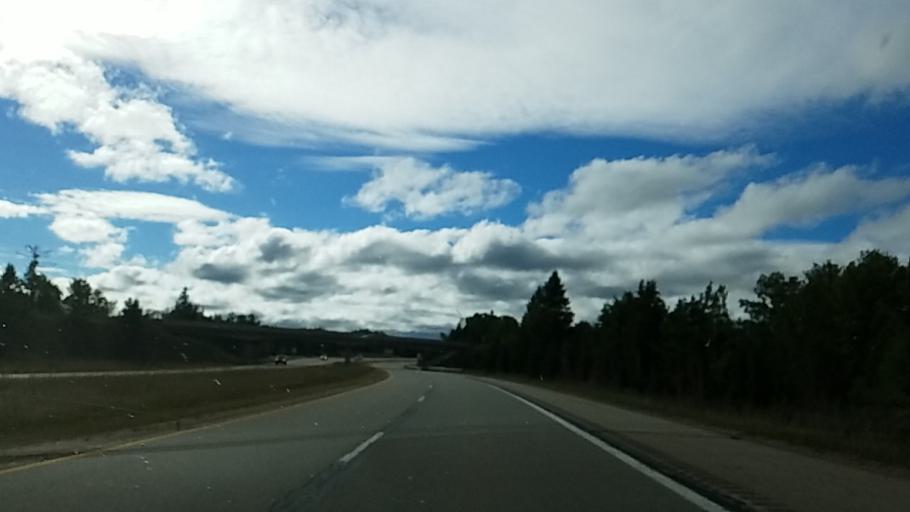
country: US
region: Michigan
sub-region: Mackinac County
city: Saint Ignace
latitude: 45.7639
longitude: -84.7337
